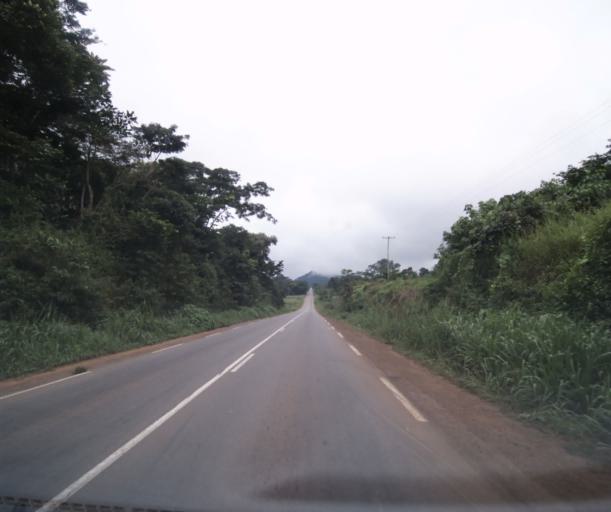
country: CM
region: Centre
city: Mbankomo
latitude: 3.7981
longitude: 11.3554
